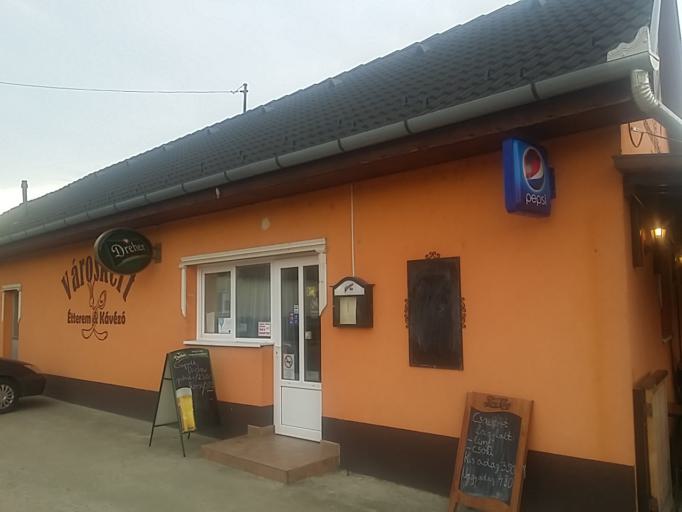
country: HU
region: Szabolcs-Szatmar-Bereg
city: Nagykallo
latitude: 47.8741
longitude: 21.8393
